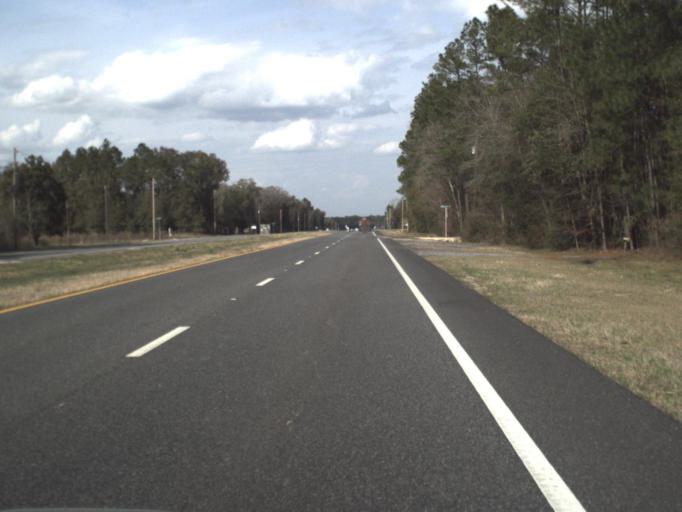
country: US
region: Florida
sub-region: Bay County
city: Youngstown
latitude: 30.5091
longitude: -85.4115
